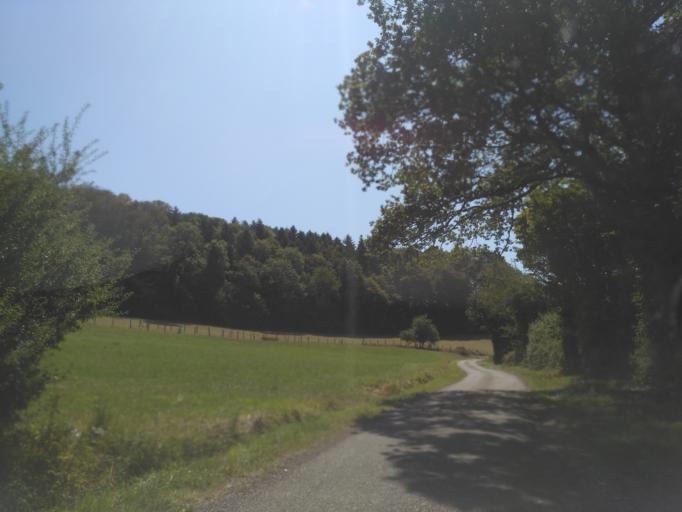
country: FR
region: Franche-Comte
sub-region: Departement de la Haute-Saone
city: Villersexel
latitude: 47.5028
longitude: 6.5283
